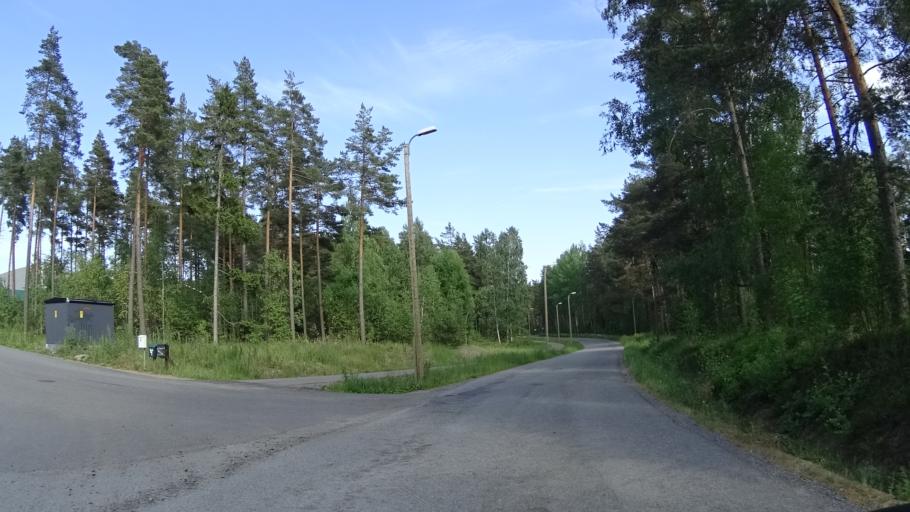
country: FI
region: Uusimaa
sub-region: Raaseporin
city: Inga
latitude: 60.0557
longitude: 23.9823
